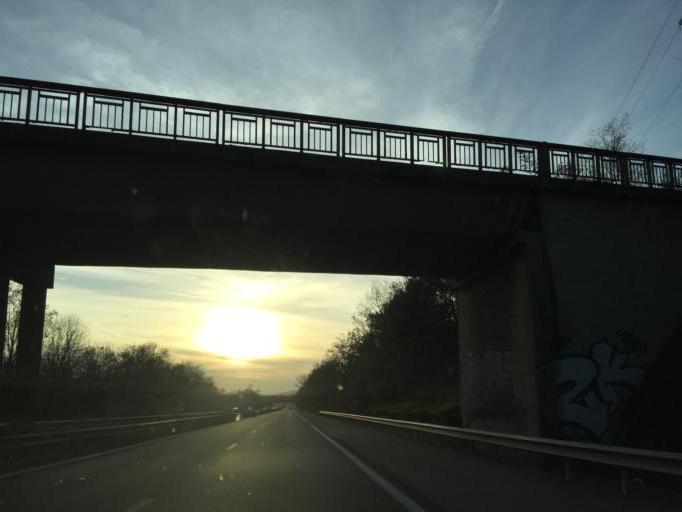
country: FR
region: Rhone-Alpes
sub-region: Departement de la Loire
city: La Grand-Croix
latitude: 45.4899
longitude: 4.5458
